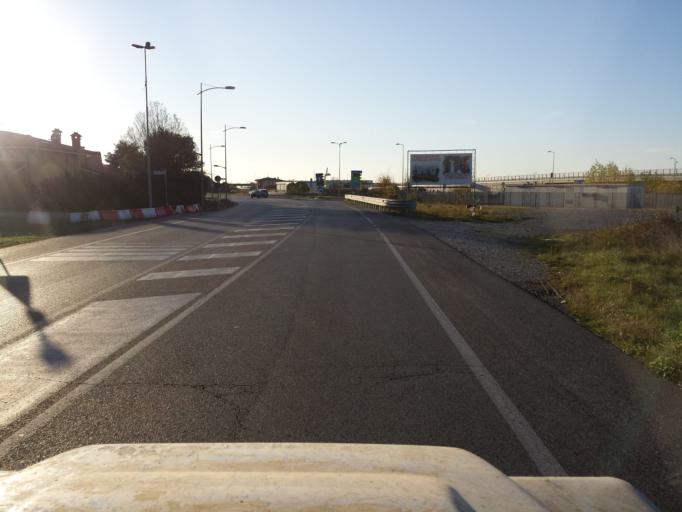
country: IT
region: Friuli Venezia Giulia
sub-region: Provincia di Gorizia
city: Villesse
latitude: 45.8687
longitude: 13.4461
